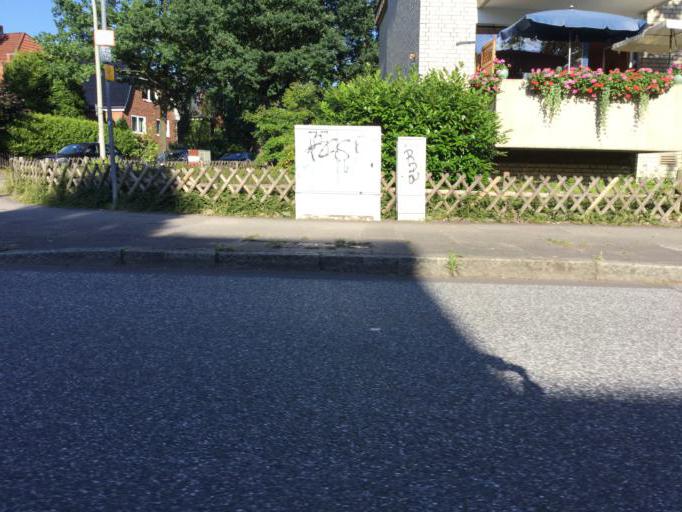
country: DE
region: Hamburg
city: Fuhlsbuettel
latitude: 53.6377
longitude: 10.0251
